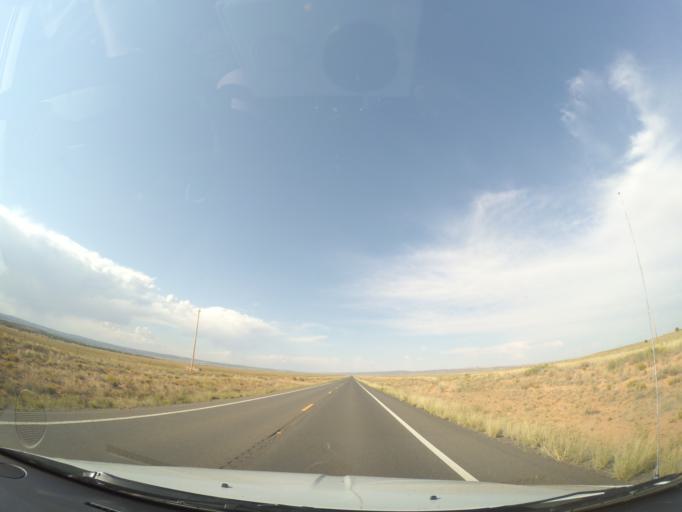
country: US
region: Arizona
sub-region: Coconino County
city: Tuba City
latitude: 36.3602
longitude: -111.4233
